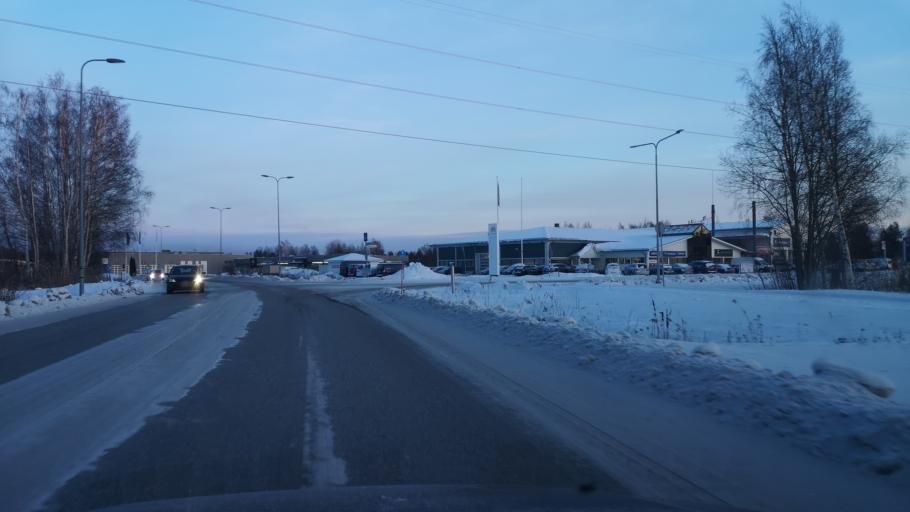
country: FI
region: Satakunta
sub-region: Pori
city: Pori
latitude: 61.4822
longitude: 21.8205
